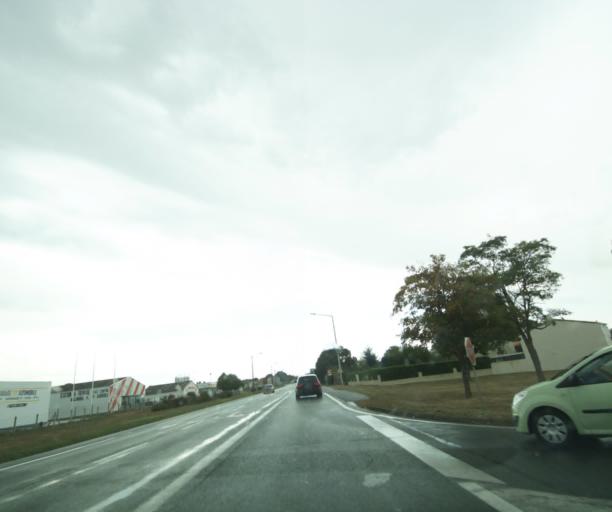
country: FR
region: Poitou-Charentes
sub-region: Departement de la Charente-Maritime
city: Tonnay-Charente
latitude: 45.9513
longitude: -0.8905
